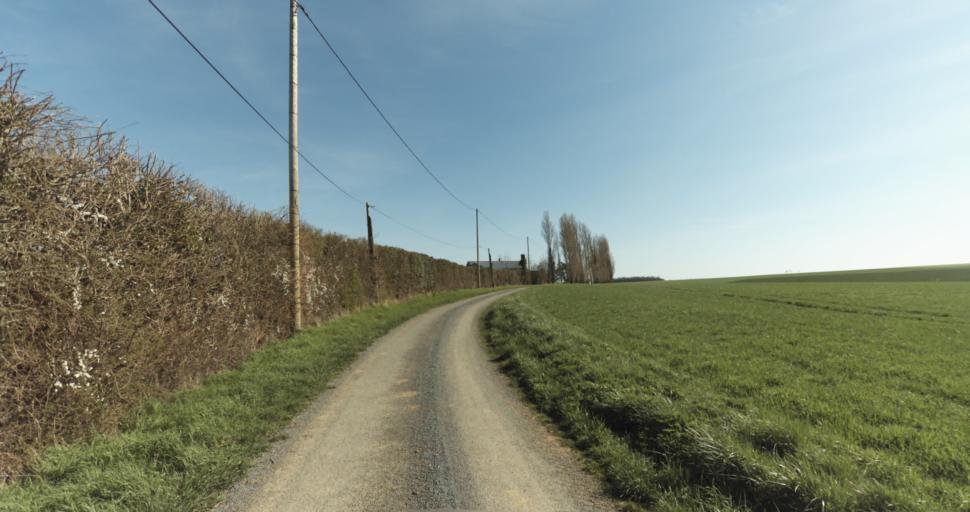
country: FR
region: Lower Normandy
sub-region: Departement du Calvados
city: Saint-Pierre-sur-Dives
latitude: 49.0035
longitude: -0.0444
